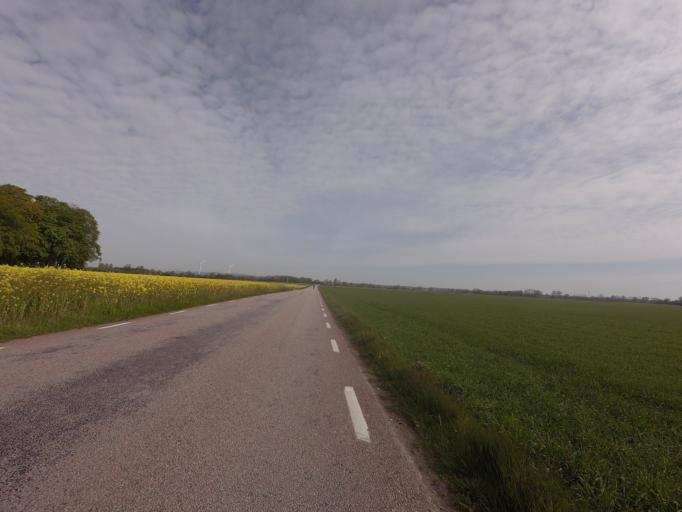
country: SE
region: Skane
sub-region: Hoganas Kommun
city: Hoganas
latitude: 56.2151
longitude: 12.5958
